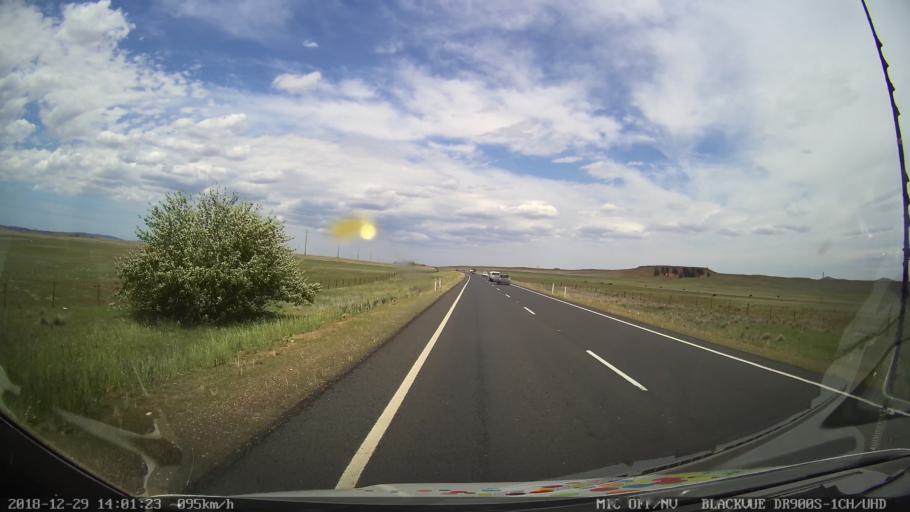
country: AU
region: New South Wales
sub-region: Cooma-Monaro
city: Cooma
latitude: -36.2748
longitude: 149.1676
